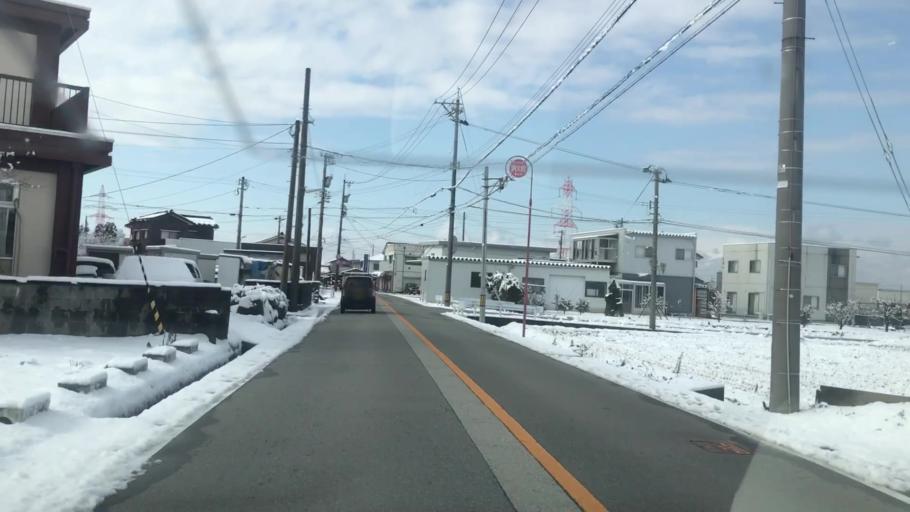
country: JP
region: Toyama
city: Toyama-shi
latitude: 36.6326
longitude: 137.2161
